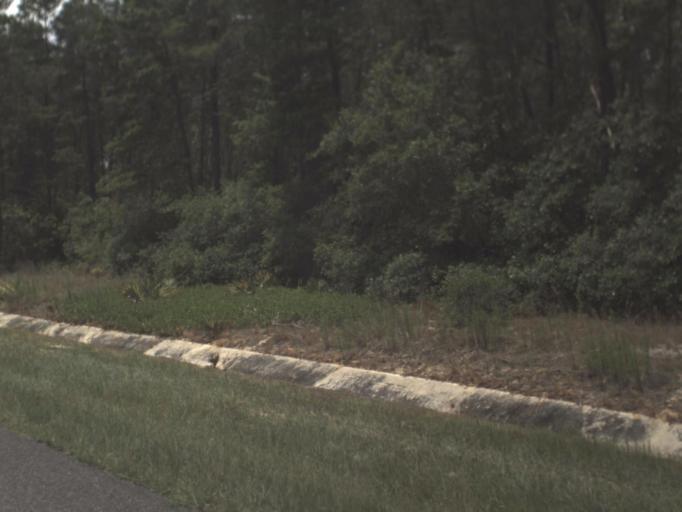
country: US
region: Florida
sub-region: Putnam County
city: Crescent City
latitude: 29.3734
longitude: -81.7358
